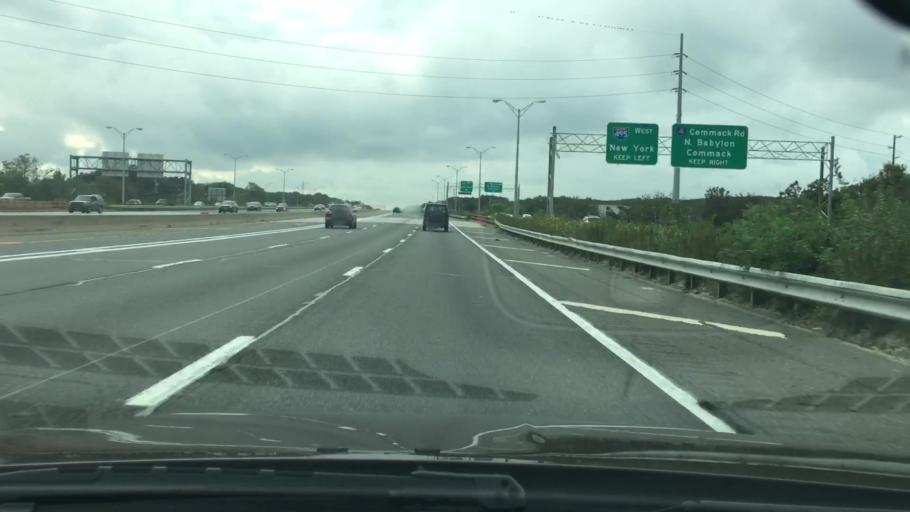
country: US
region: New York
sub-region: Suffolk County
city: Commack
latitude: 40.8051
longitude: -73.2865
